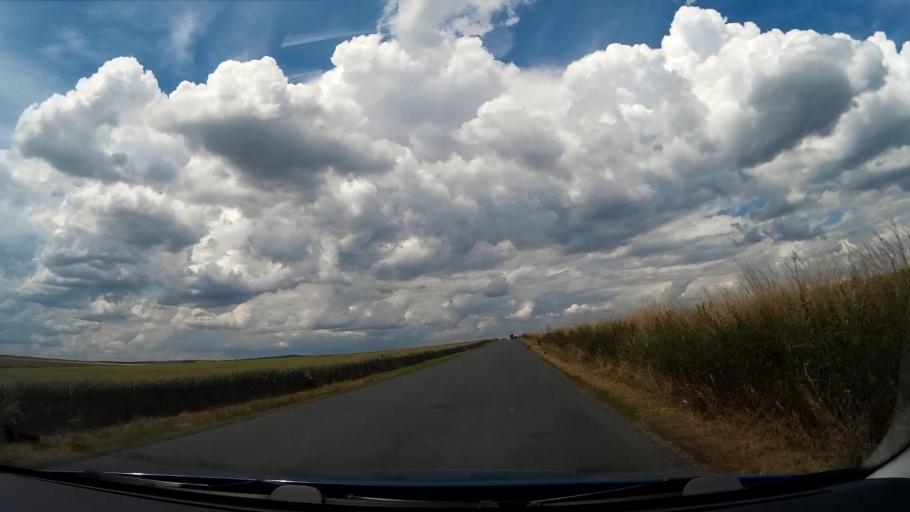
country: CZ
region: South Moravian
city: Orechov
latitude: 49.0870
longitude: 16.5335
